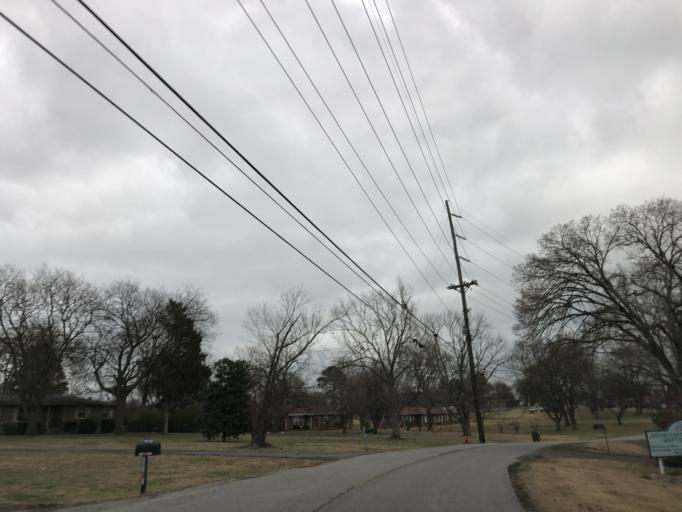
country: US
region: Tennessee
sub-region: Davidson County
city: Goodlettsville
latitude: 36.2969
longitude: -86.6935
